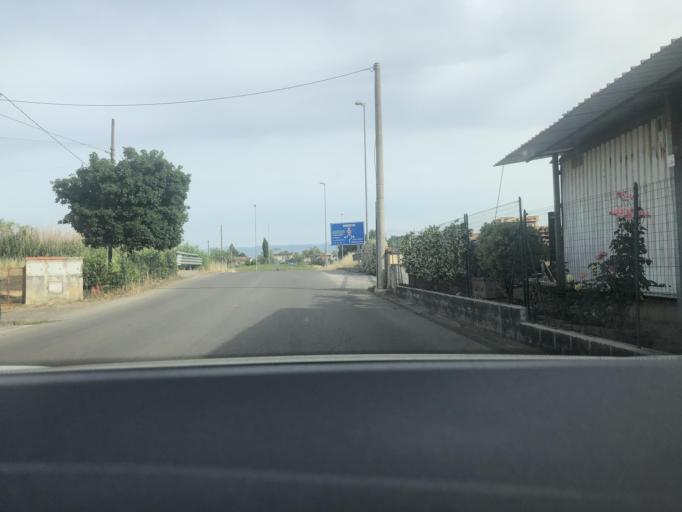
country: IT
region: Tuscany
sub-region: Provincia di Pistoia
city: San Rocco
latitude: 43.8141
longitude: 10.8616
